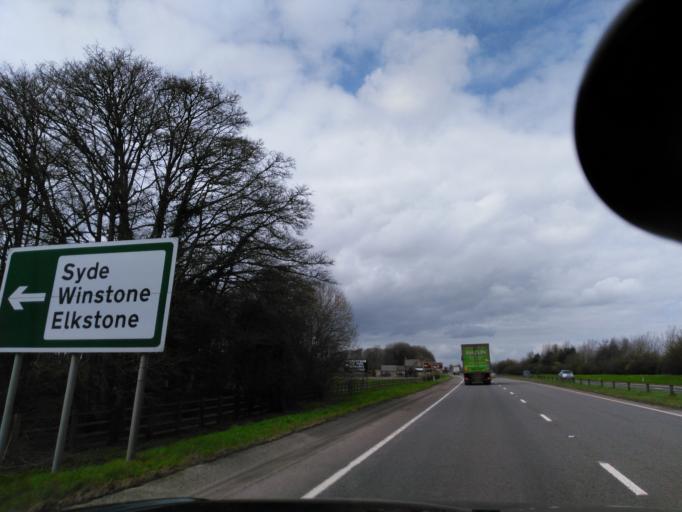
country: GB
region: England
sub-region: Gloucestershire
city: Coates
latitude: 51.7939
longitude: -2.0482
